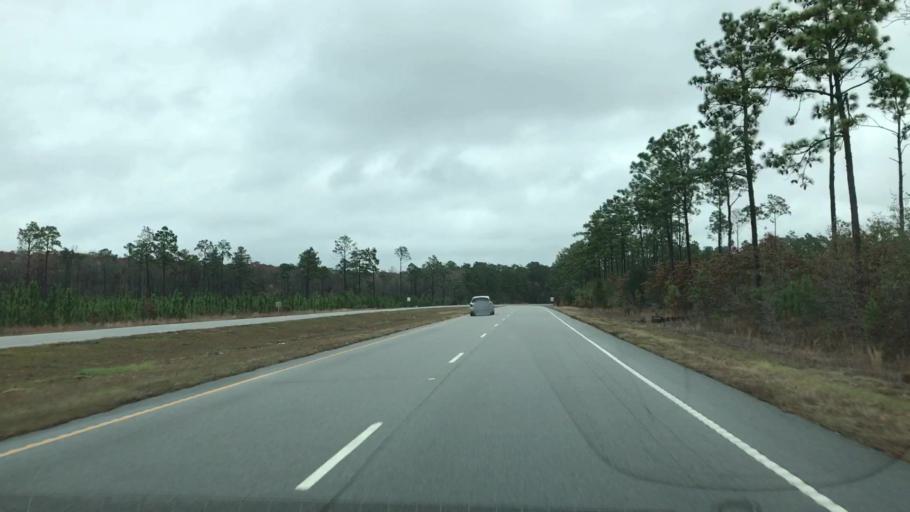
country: US
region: South Carolina
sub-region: Georgetown County
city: Georgetown
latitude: 33.1766
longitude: -79.4152
